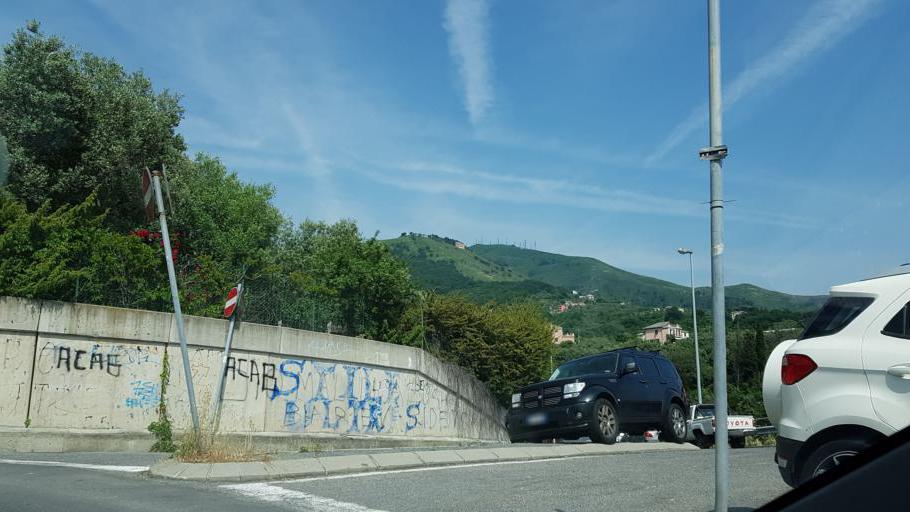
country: IT
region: Liguria
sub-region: Provincia di Genova
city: Bogliasco
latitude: 44.4024
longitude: 8.9956
